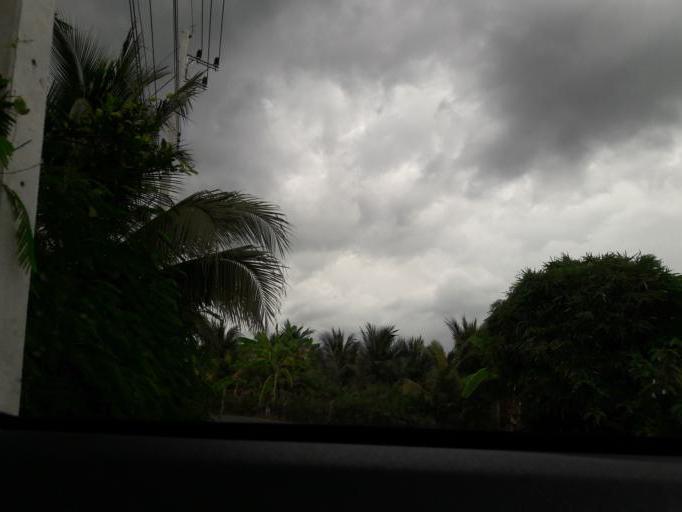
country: TH
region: Ratchaburi
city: Damnoen Saduak
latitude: 13.5731
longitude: 99.9841
